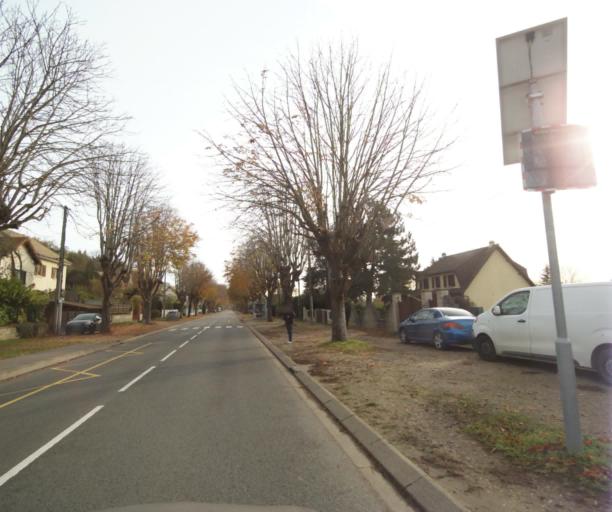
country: FR
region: Ile-de-France
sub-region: Departement des Yvelines
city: Vernouillet
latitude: 48.9933
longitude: 1.9877
